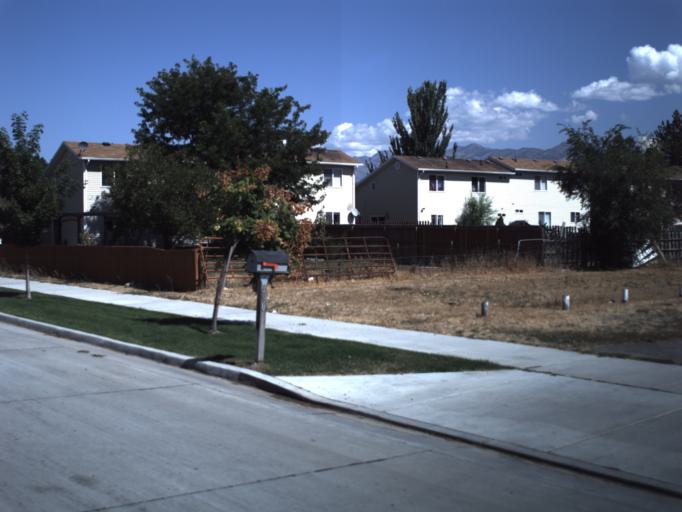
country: US
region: Utah
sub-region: Cache County
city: Logan
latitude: 41.7229
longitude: -111.8599
